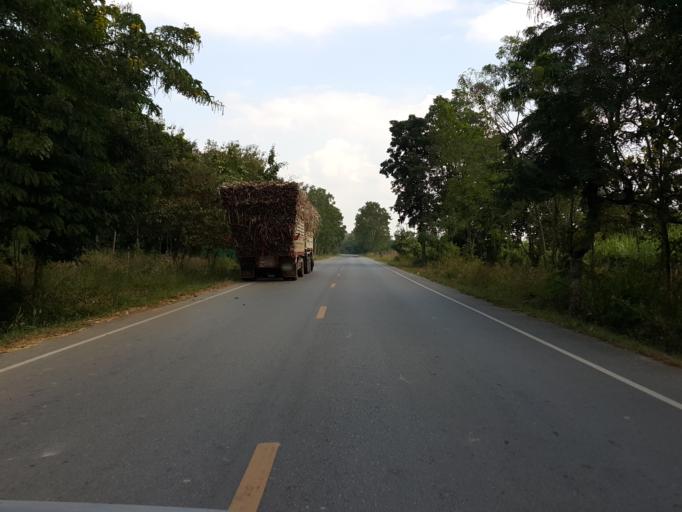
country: TH
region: Sukhothai
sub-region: Amphoe Si Satchanalai
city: Si Satchanalai
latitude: 17.4587
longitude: 99.6738
